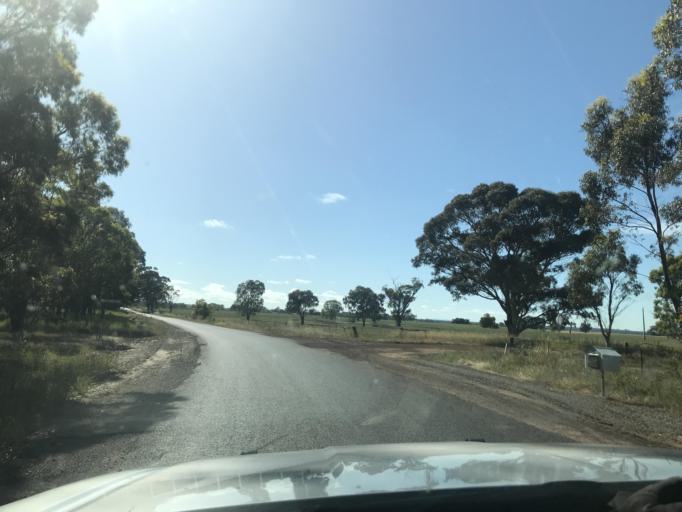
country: AU
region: Victoria
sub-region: Horsham
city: Horsham
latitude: -37.0399
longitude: 141.7308
